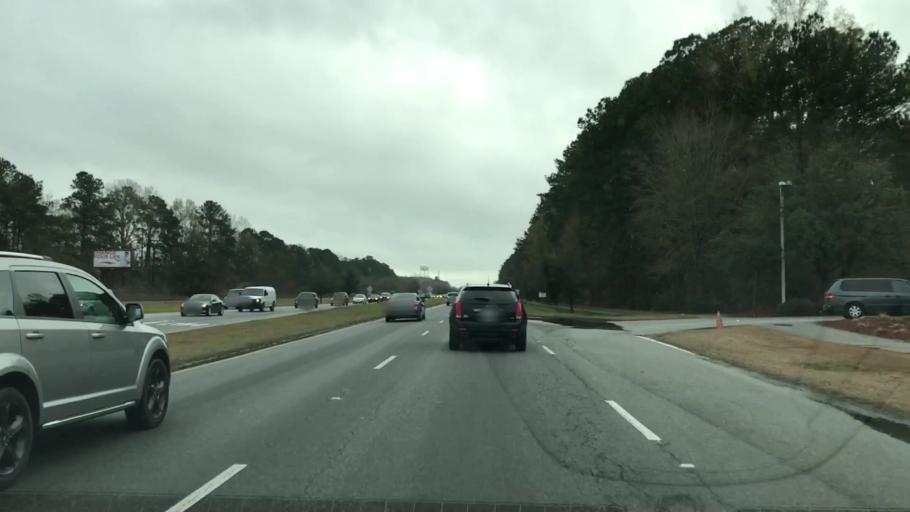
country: US
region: South Carolina
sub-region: Berkeley County
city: Goose Creek
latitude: 33.0179
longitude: -80.0363
